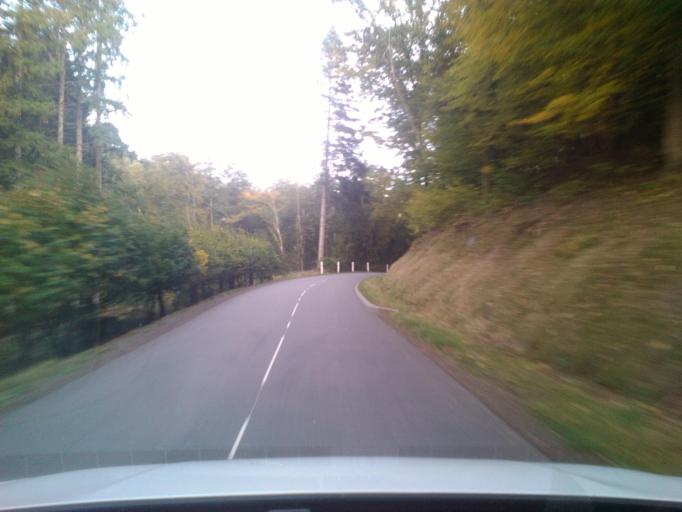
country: FR
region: Lorraine
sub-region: Departement des Vosges
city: Taintrux
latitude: 48.2460
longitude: 6.9164
